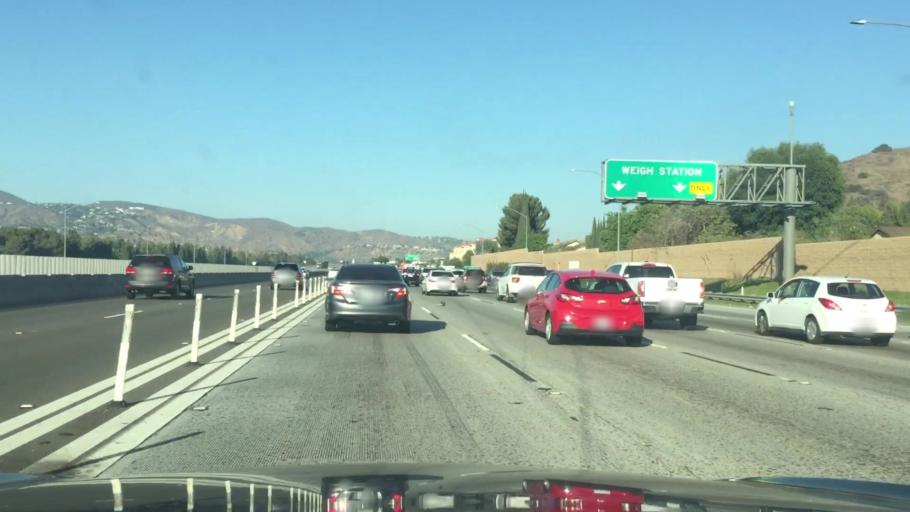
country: US
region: California
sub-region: Orange County
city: Yorba Linda
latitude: 33.8654
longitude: -117.7645
